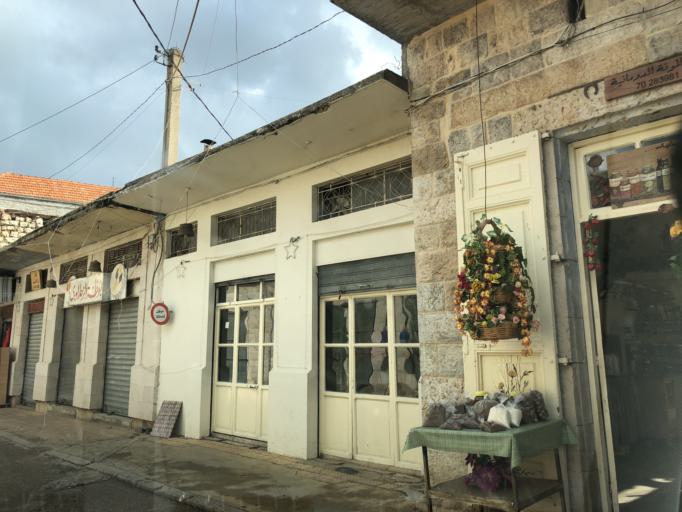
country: LB
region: Liban-Nord
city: Amioun
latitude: 34.2054
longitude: 35.8391
